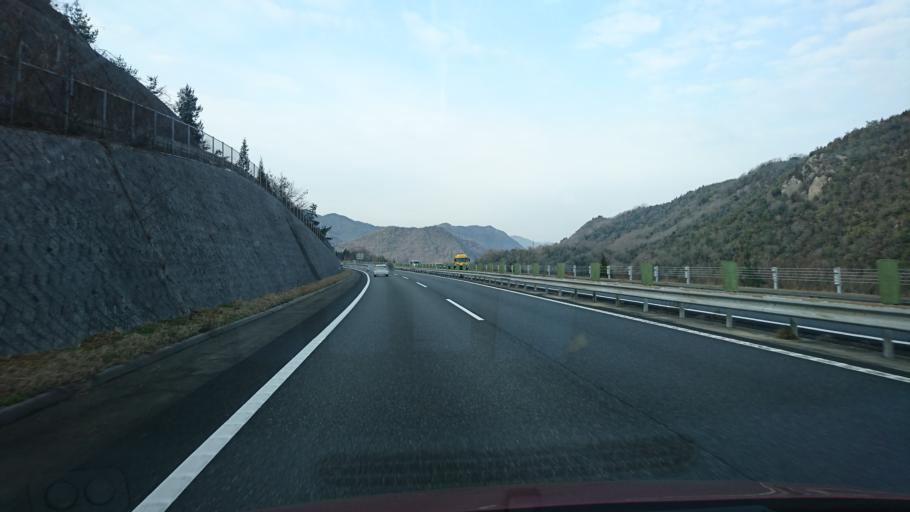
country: JP
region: Hyogo
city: Kariya
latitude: 34.7946
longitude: 134.1821
